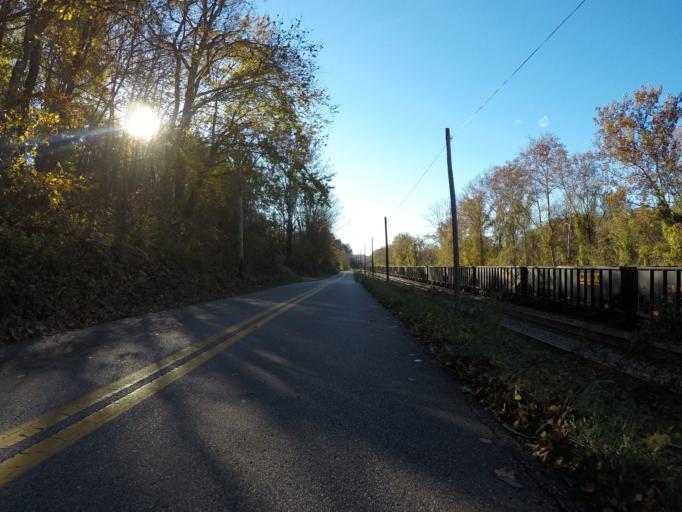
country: US
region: West Virginia
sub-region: Wayne County
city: Ceredo
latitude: 38.3940
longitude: -82.5438
